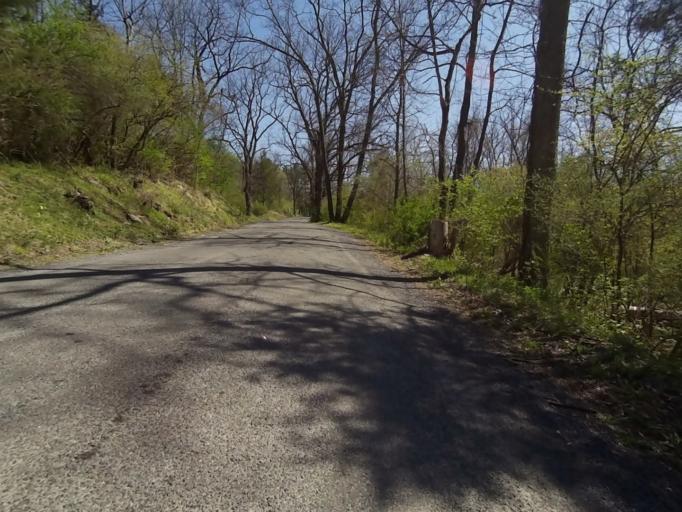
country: US
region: Pennsylvania
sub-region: Centre County
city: Houserville
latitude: 40.8860
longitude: -77.8395
